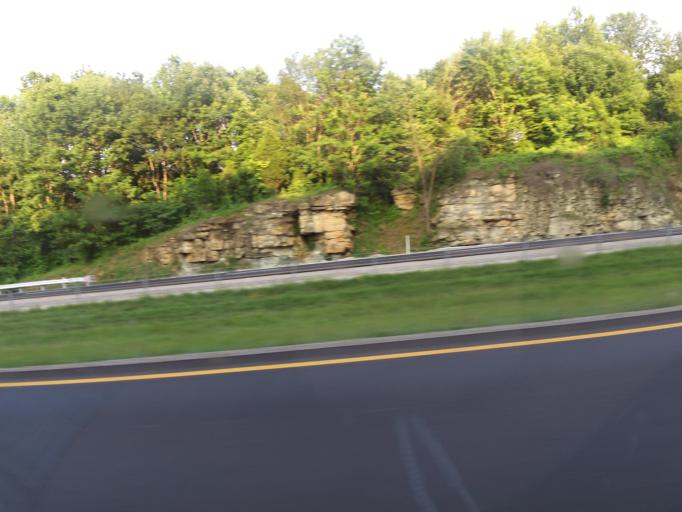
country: US
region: Kentucky
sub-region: Rockcastle County
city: Brodhead
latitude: 37.4364
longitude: -84.3416
